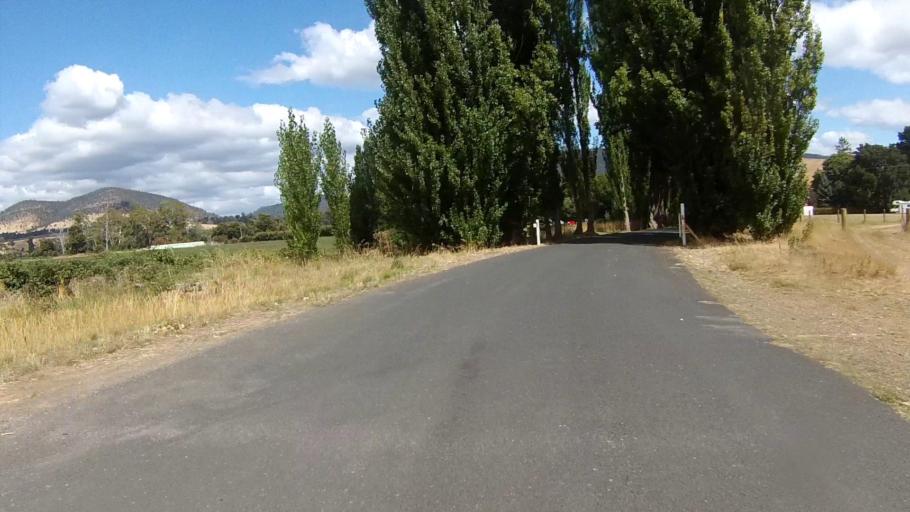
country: AU
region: Tasmania
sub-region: Derwent Valley
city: New Norfolk
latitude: -42.7528
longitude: 146.9717
